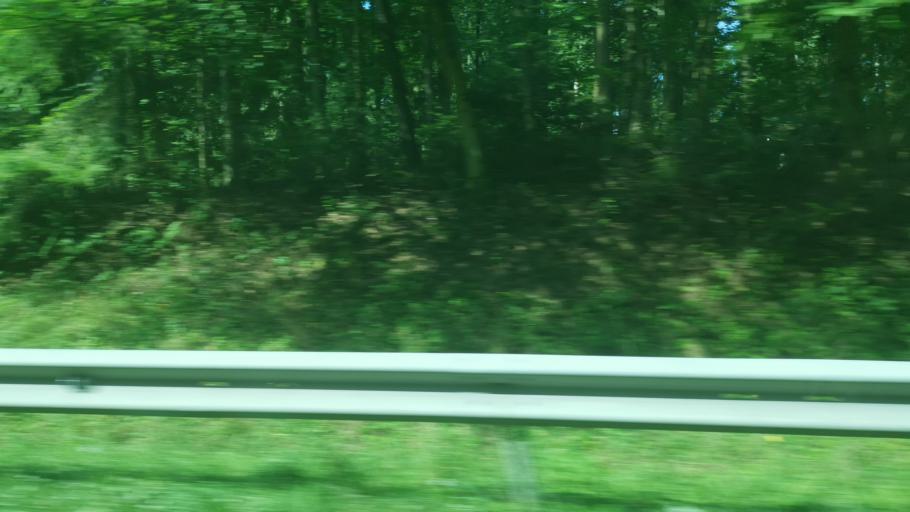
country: DE
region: Bavaria
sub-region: Upper Palatinate
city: Pemfling
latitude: 49.2805
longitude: 12.6250
